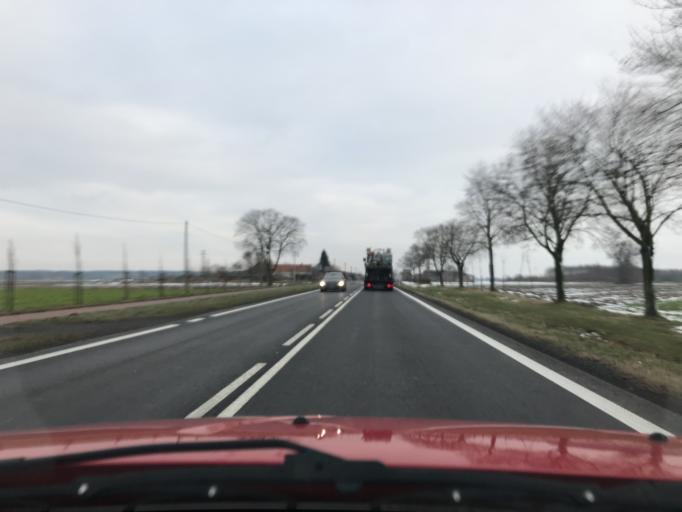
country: PL
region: Greater Poland Voivodeship
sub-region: Powiat pleszewski
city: Goluchow
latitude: 51.8725
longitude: 17.8917
